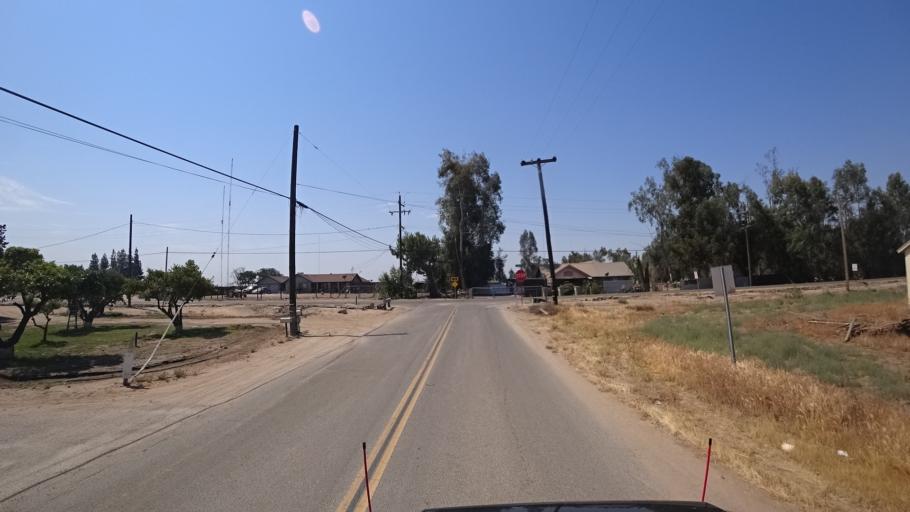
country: US
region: California
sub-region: Fresno County
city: West Park
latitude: 36.7143
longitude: -119.8358
